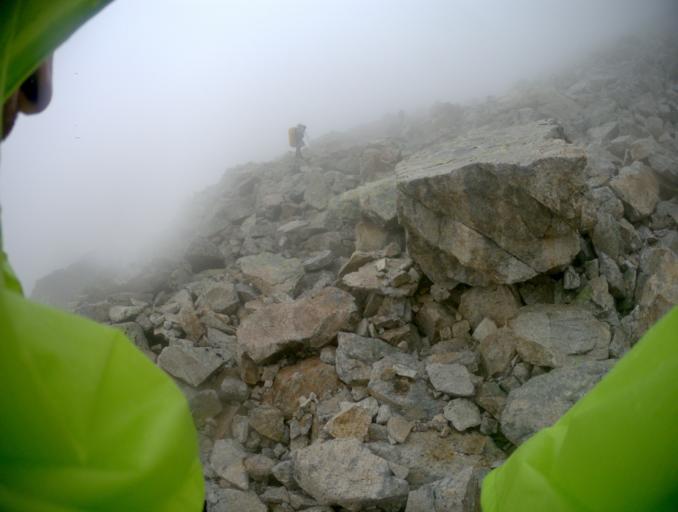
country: RU
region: Karachayevo-Cherkesiya
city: Uchkulan
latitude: 43.2832
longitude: 42.1030
